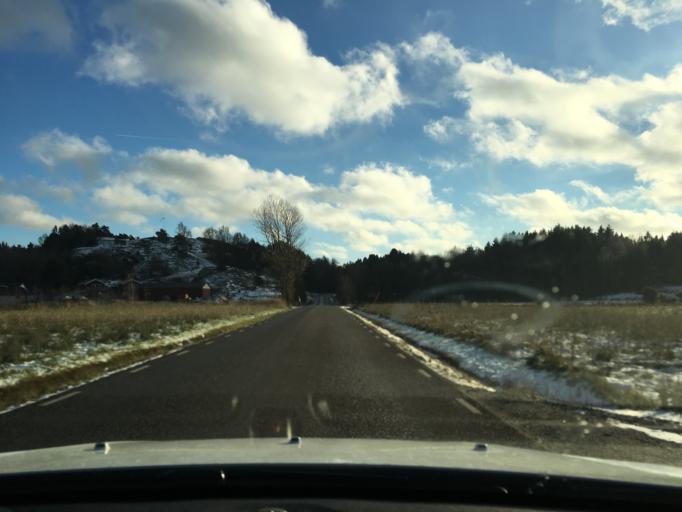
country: SE
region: Vaestra Goetaland
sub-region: Tjorns Kommun
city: Myggenas
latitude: 58.0425
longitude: 11.7313
